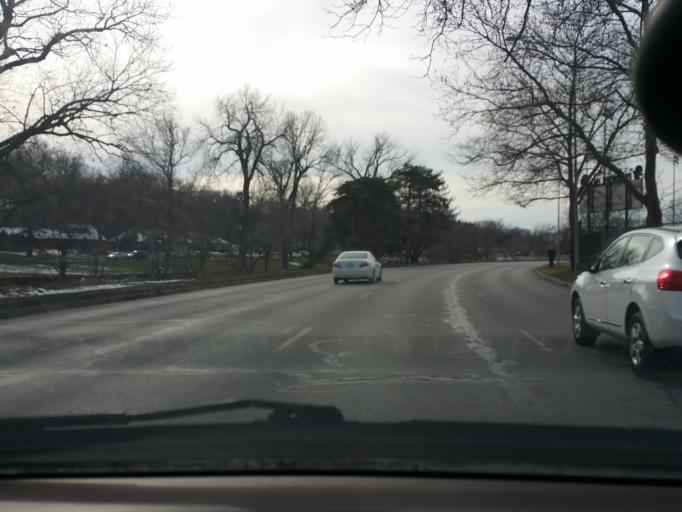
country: US
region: Kansas
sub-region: Johnson County
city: Westwood
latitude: 39.0347
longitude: -94.6027
